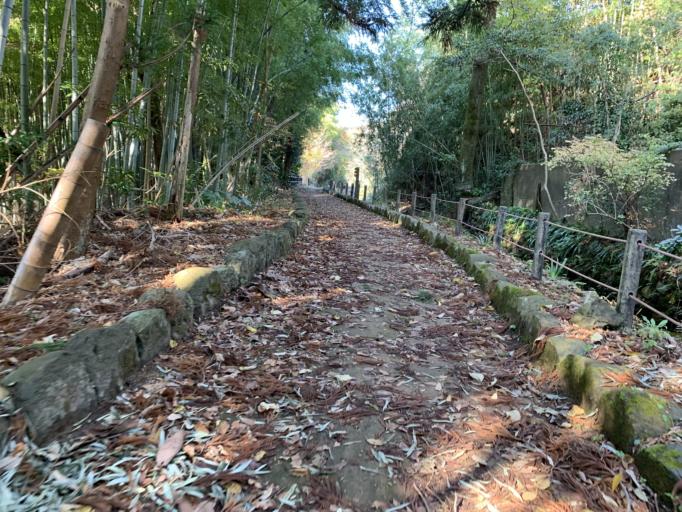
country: JP
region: Ishikawa
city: Nonoichi
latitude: 36.5345
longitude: 136.6885
